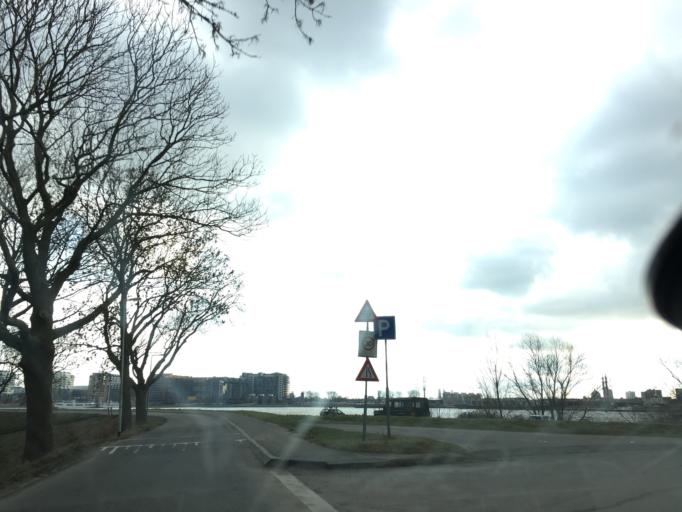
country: NL
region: South Holland
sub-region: Gemeente Rotterdam
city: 's-Gravenland
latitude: 51.9047
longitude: 4.5230
